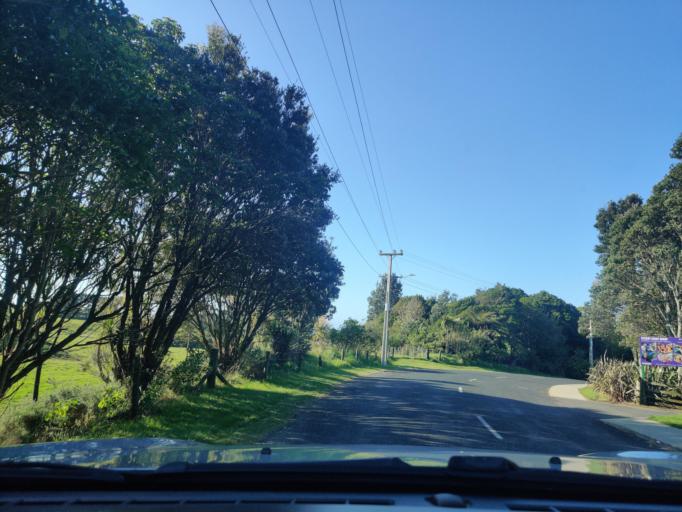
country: NZ
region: Taranaki
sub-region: New Plymouth District
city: New Plymouth
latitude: -39.0446
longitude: 174.1126
